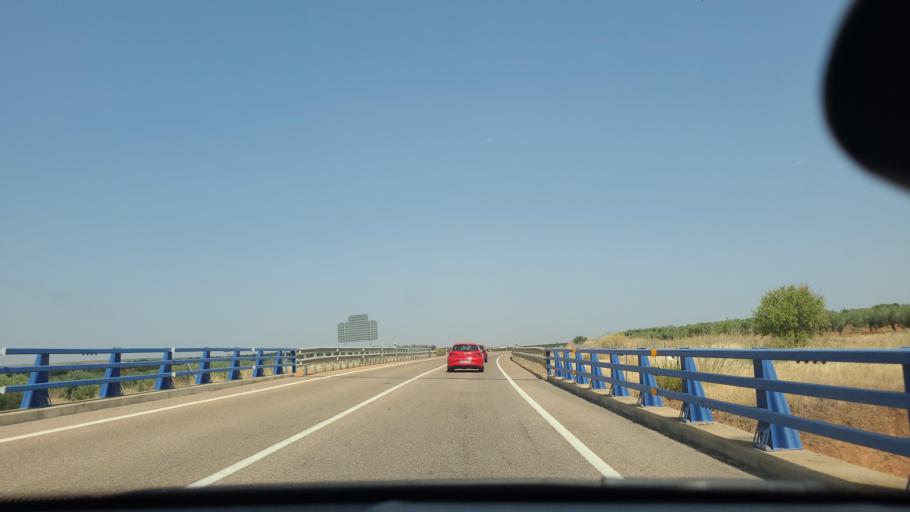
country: ES
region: Extremadura
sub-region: Provincia de Badajoz
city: La Albuera
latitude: 38.7149
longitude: -6.8336
